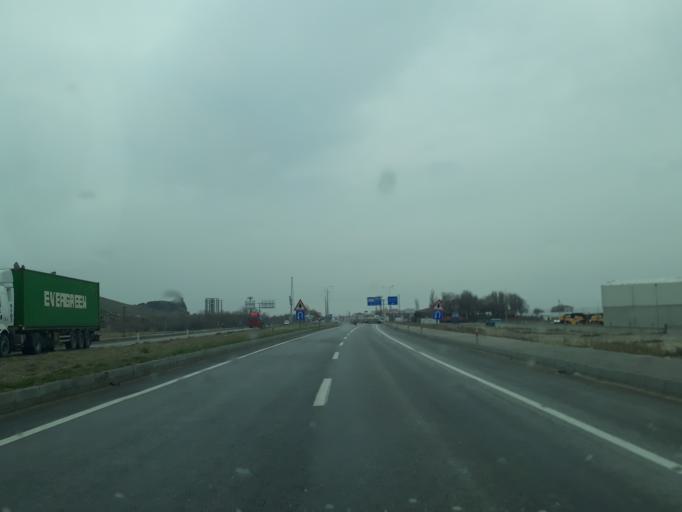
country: TR
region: Konya
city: Karapinar
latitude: 37.7147
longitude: 33.5845
